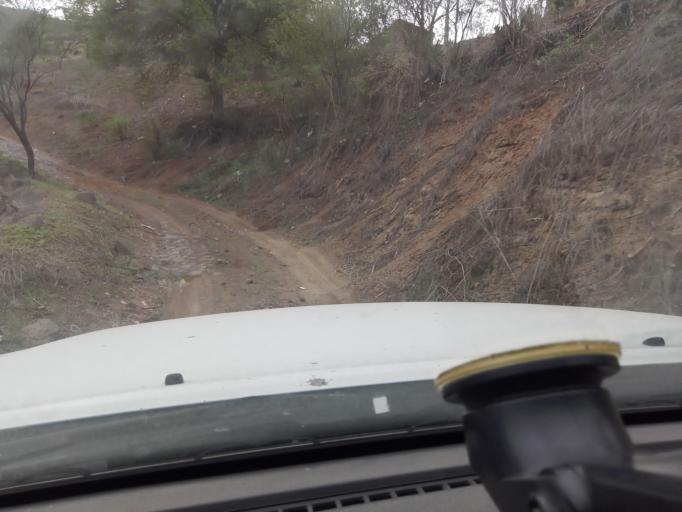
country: CV
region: Sao Salvador do Mundo
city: Picos
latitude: 15.1415
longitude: -23.6353
